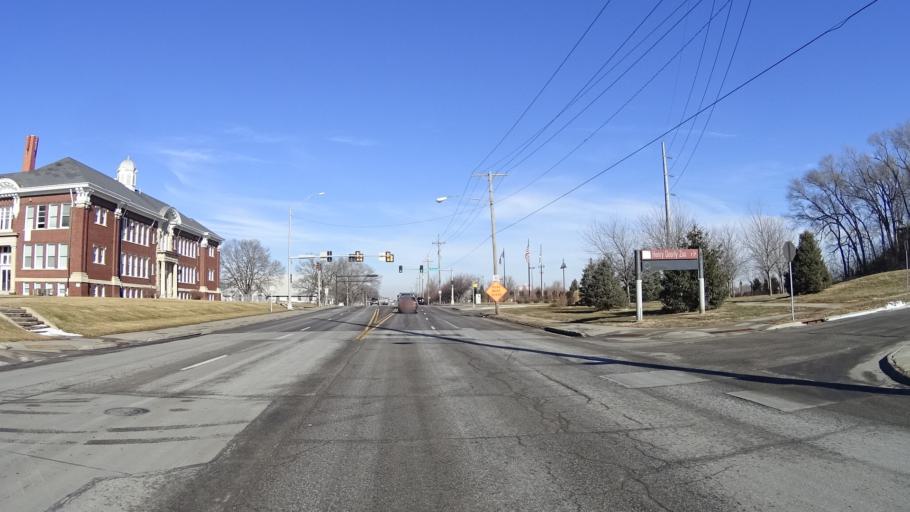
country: US
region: Nebraska
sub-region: Douglas County
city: Omaha
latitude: 41.2227
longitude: -95.9333
